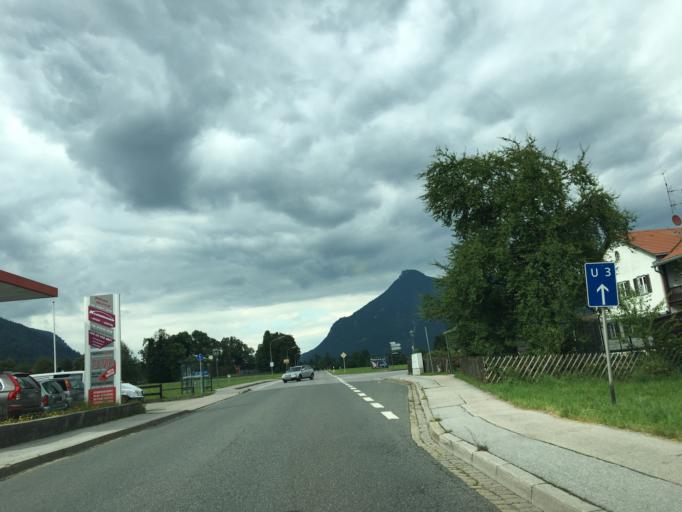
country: DE
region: Bavaria
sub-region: Upper Bavaria
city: Oberaudorf
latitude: 47.6521
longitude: 12.1729
